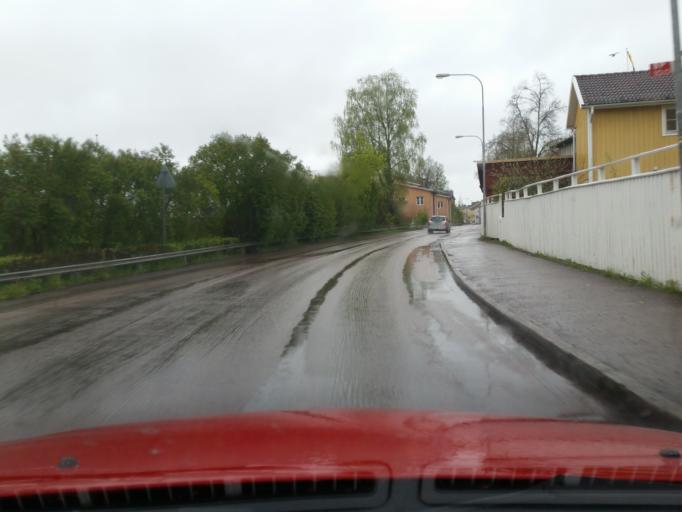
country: SE
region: Dalarna
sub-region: Hedemora Kommun
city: Hedemora
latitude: 60.2812
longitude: 15.9814
